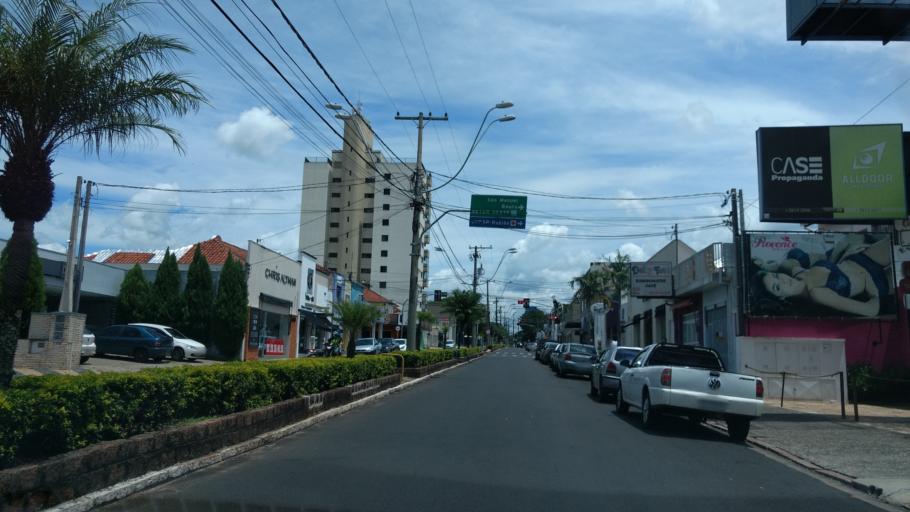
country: BR
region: Sao Paulo
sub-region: Botucatu
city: Botucatu
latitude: -22.8911
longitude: -48.4449
